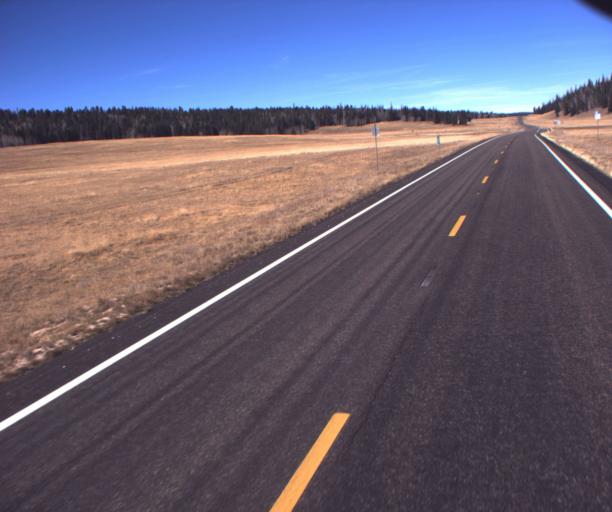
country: US
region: Arizona
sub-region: Coconino County
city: Grand Canyon
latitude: 36.3982
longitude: -112.1288
